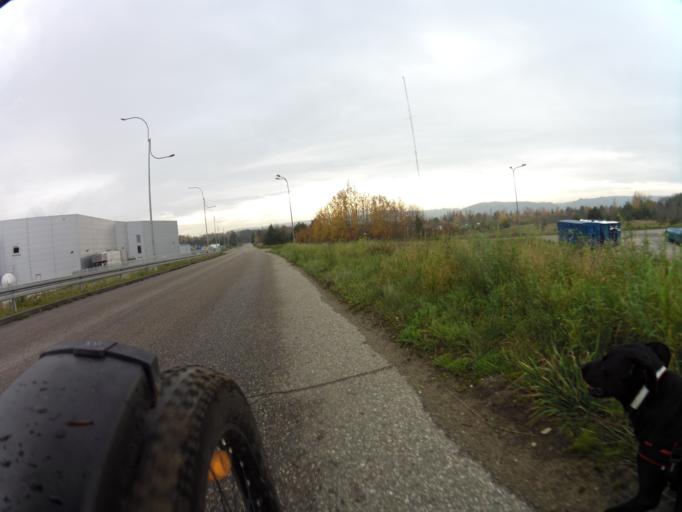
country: PL
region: Pomeranian Voivodeship
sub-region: Powiat pucki
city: Krokowa
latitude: 54.7388
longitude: 18.0944
